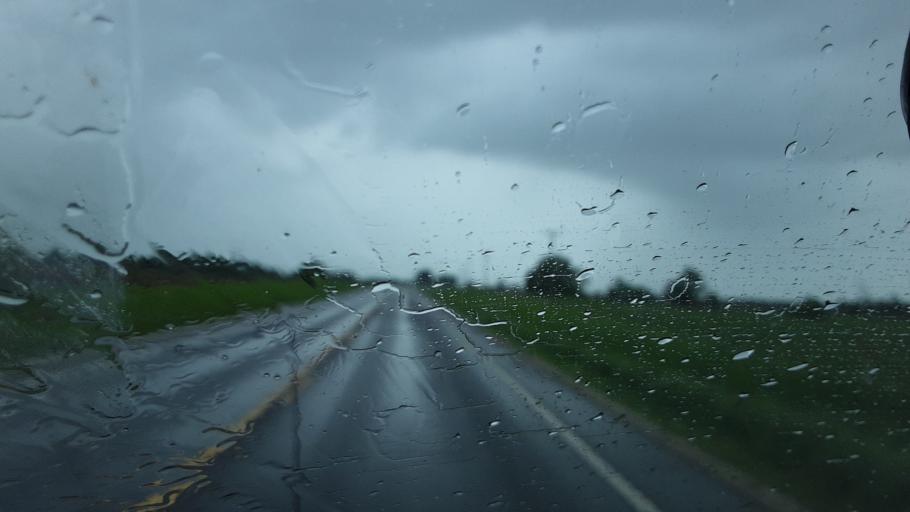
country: US
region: Missouri
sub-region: Monroe County
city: Paris
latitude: 39.4789
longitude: -92.1798
